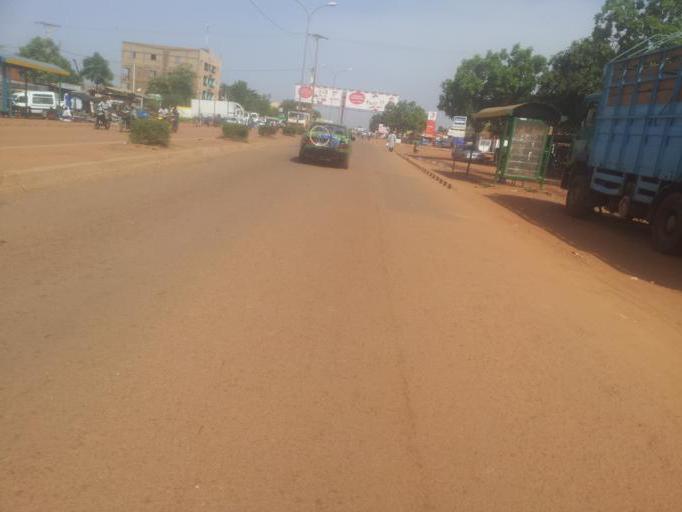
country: BF
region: Centre
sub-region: Kadiogo Province
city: Ouagadougou
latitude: 12.3889
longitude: -1.5718
